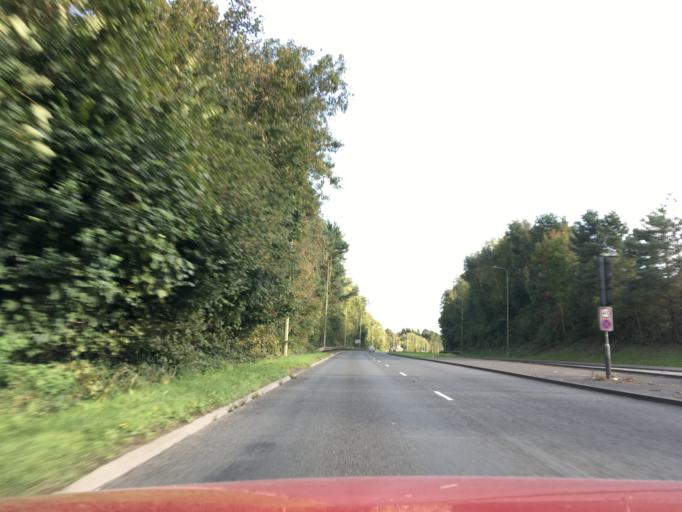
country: GB
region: Wales
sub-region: Rhondda Cynon Taf
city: Llantrisant
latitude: 51.5302
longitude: -3.3691
